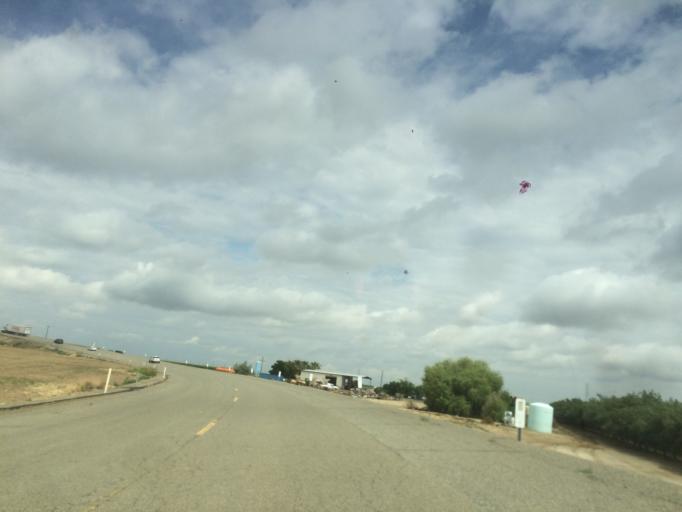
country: US
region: California
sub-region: Fresno County
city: Coalinga
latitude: 36.3681
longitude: -120.3311
